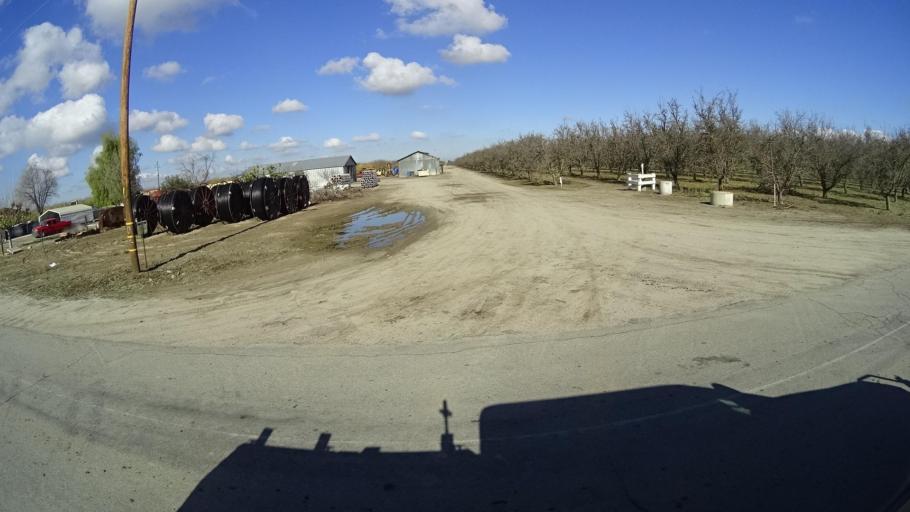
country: US
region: California
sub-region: Kern County
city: McFarland
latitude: 35.6887
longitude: -119.3210
